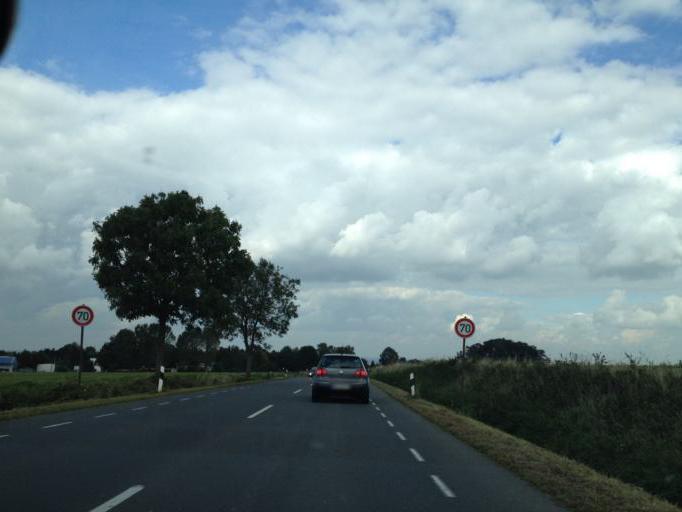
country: DE
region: North Rhine-Westphalia
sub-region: Regierungsbezirk Arnsberg
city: Soest
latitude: 51.5255
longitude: 8.0763
